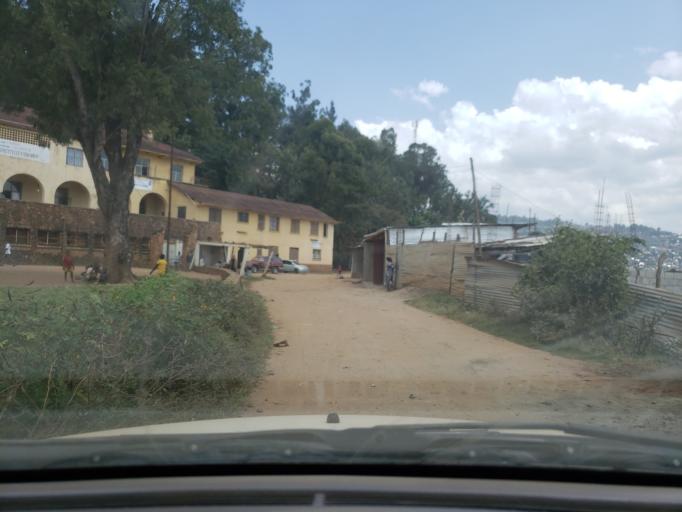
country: CD
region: South Kivu
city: Bukavu
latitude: -2.4945
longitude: 28.8620
